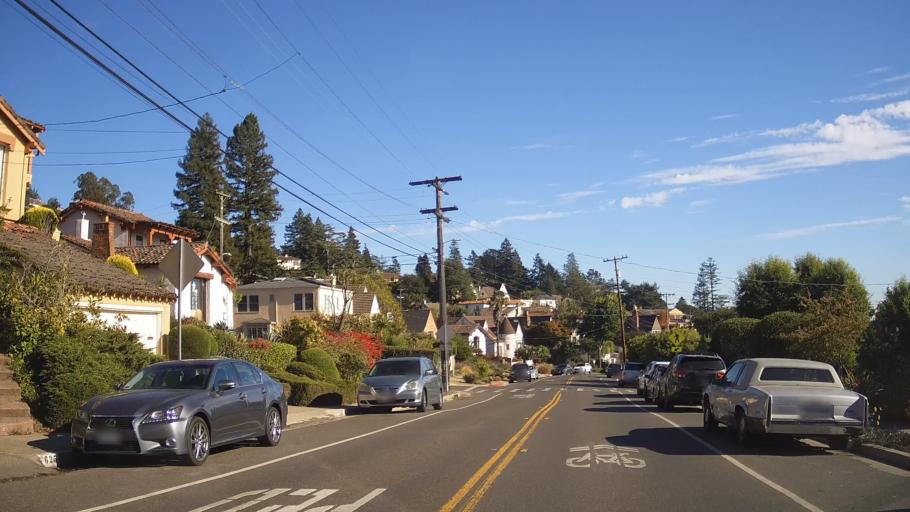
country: US
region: California
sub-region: Contra Costa County
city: Kensington
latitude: 37.8991
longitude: -122.2710
